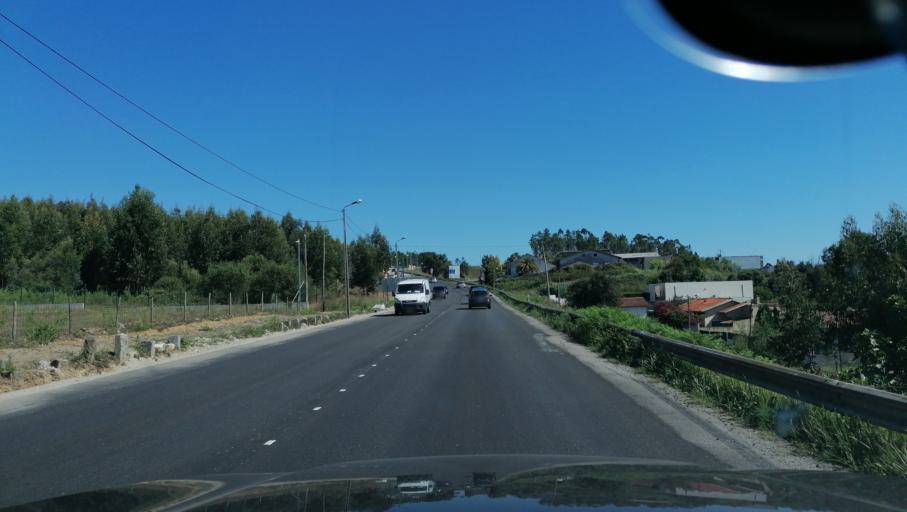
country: PT
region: Aveiro
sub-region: Santa Maria da Feira
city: Arrifana
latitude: 40.9270
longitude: -8.5087
